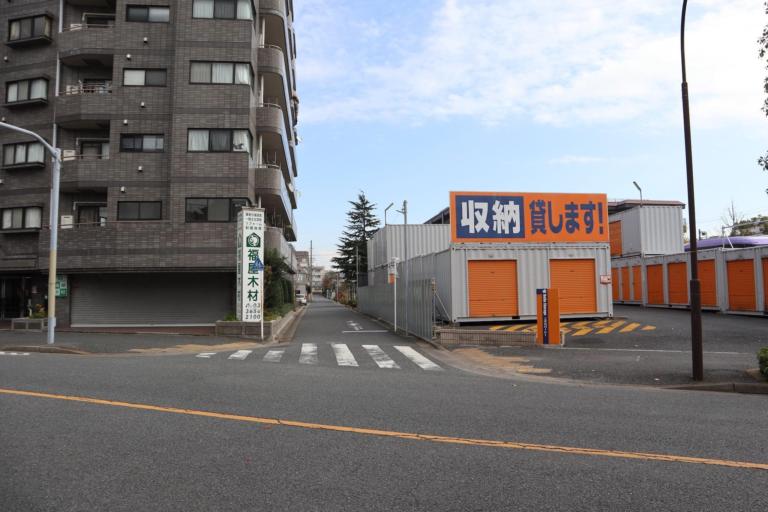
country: JP
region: Tokyo
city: Urayasu
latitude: 35.6822
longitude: 139.8746
